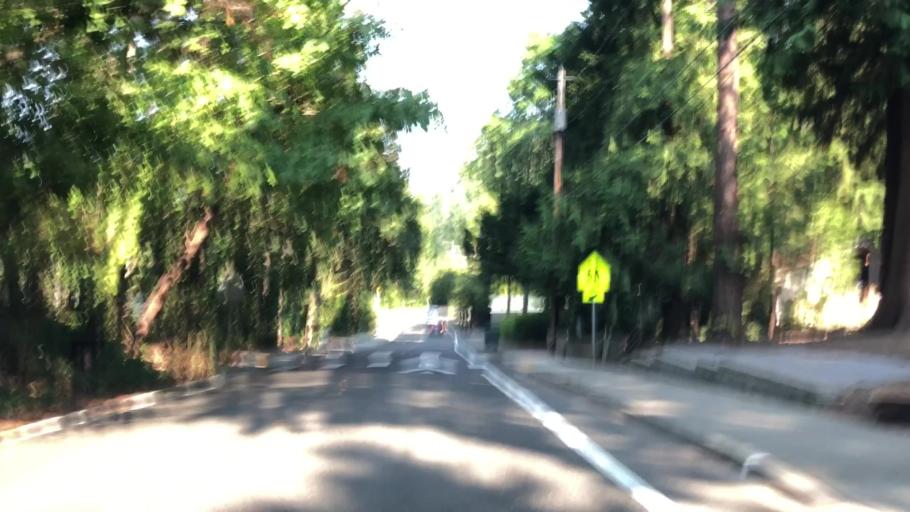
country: US
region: Washington
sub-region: King County
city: Bellevue
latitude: 47.5881
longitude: -122.1984
